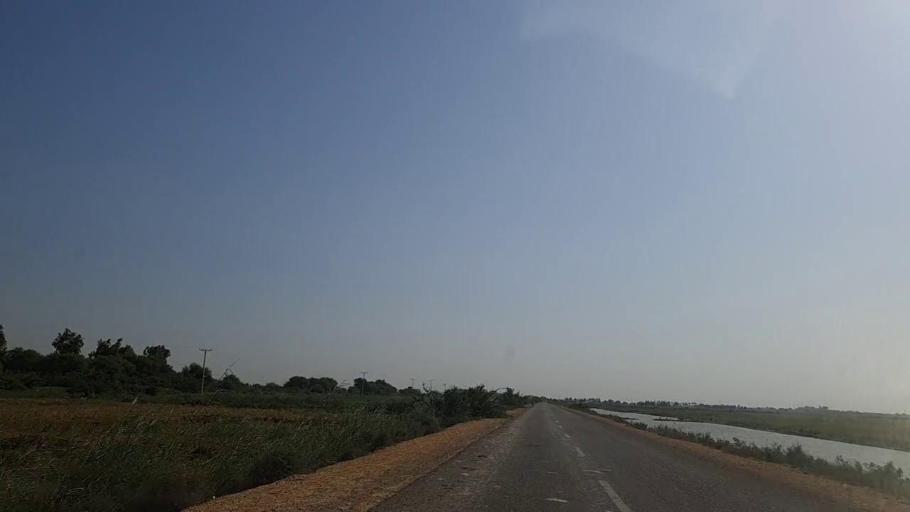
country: PK
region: Sindh
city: Jati
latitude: 24.5000
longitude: 68.2747
